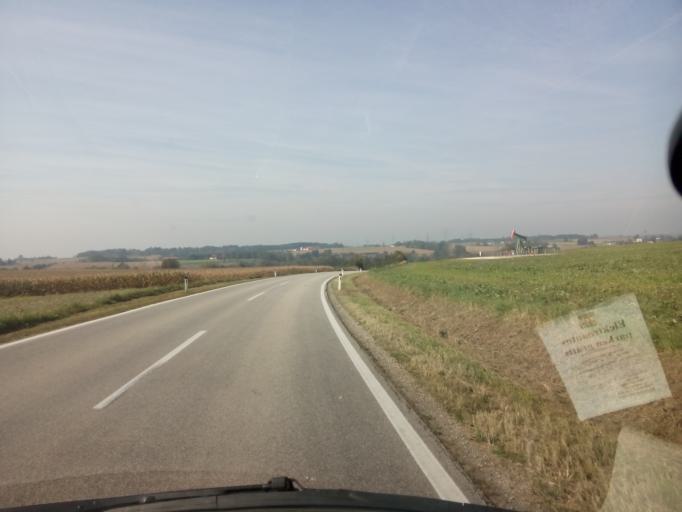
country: AT
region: Upper Austria
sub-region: Wels-Land
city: Sattledt
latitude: 48.0751
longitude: 14.0337
